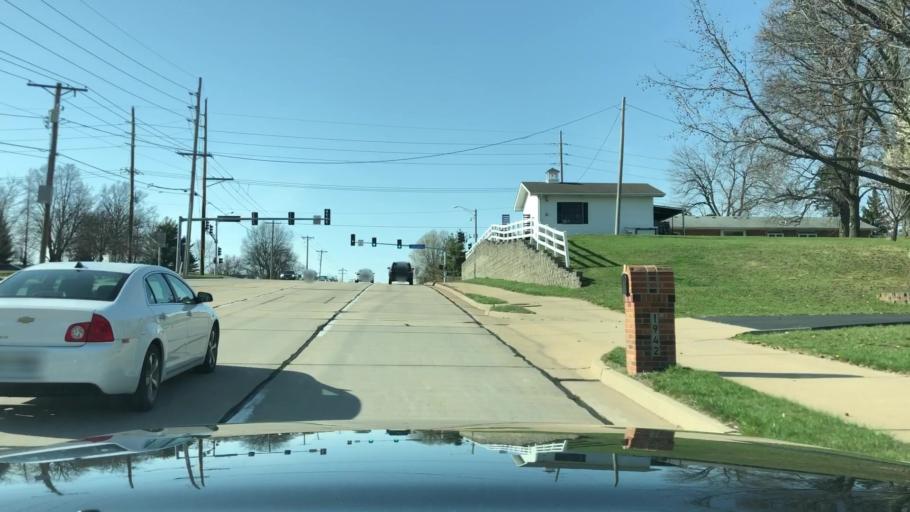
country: US
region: Missouri
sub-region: Saint Charles County
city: Saint Charles
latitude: 38.7718
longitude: -90.5493
